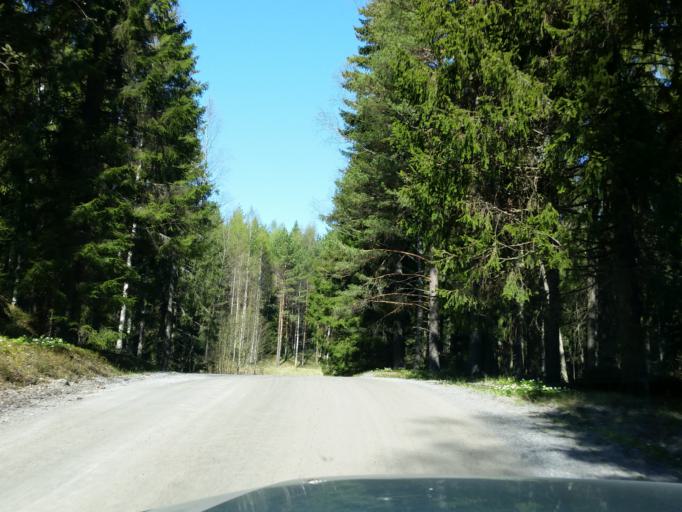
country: FI
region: Uusimaa
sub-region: Helsinki
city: Karjalohja
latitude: 60.1765
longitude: 23.6421
